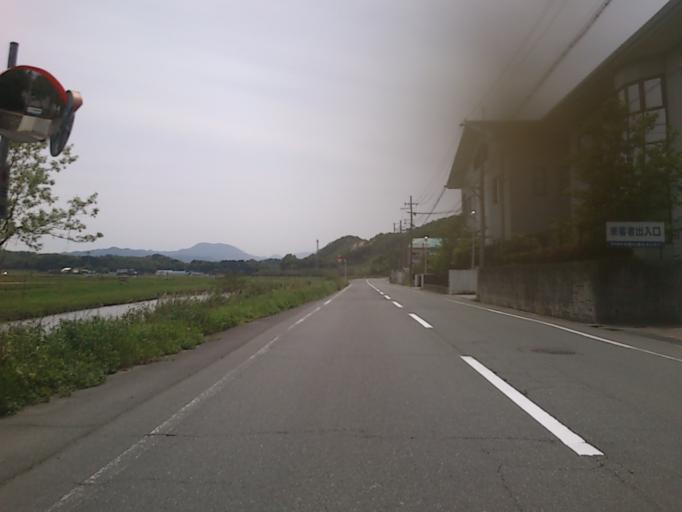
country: JP
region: Kyoto
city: Miyazu
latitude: 35.6517
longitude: 135.0894
